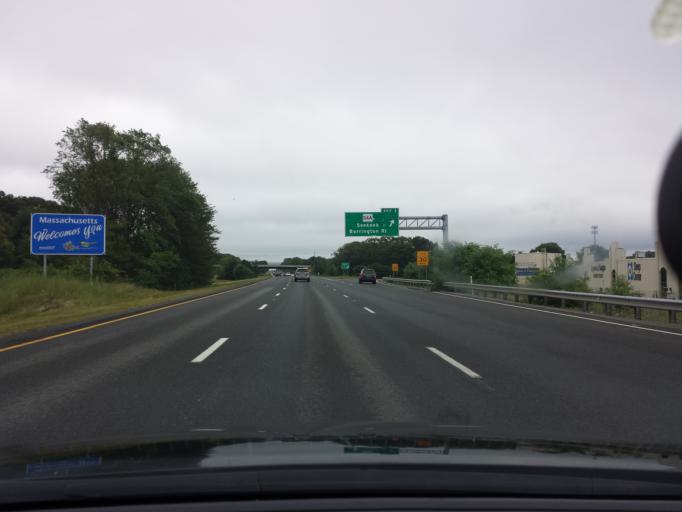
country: US
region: Massachusetts
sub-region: Bristol County
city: Seekonk
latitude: 41.8044
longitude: -71.3354
